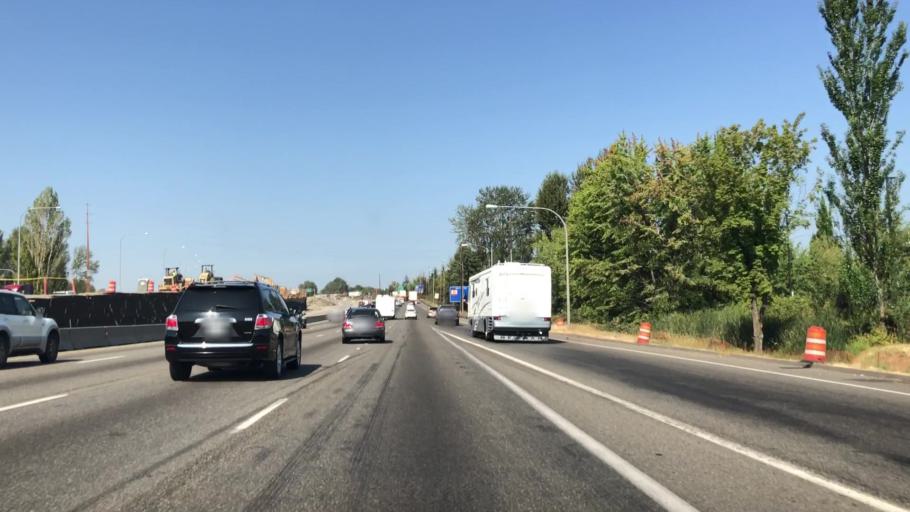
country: US
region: Washington
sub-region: Pierce County
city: Fife
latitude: 47.2419
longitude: -122.3897
